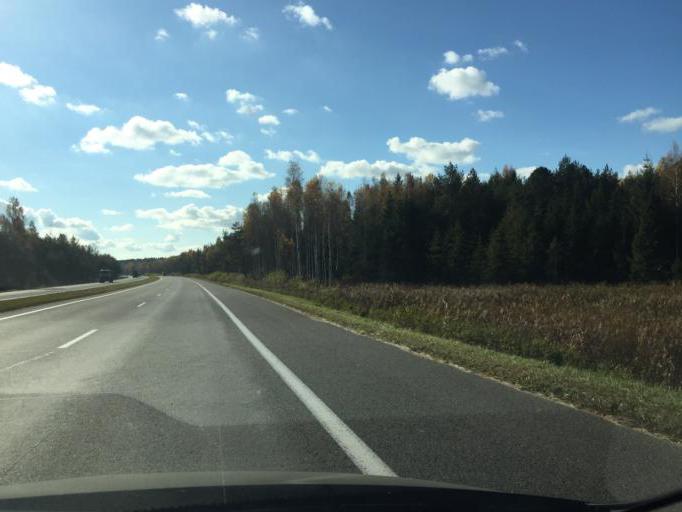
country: BY
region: Minsk
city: Slabada
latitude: 53.9408
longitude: 27.9664
